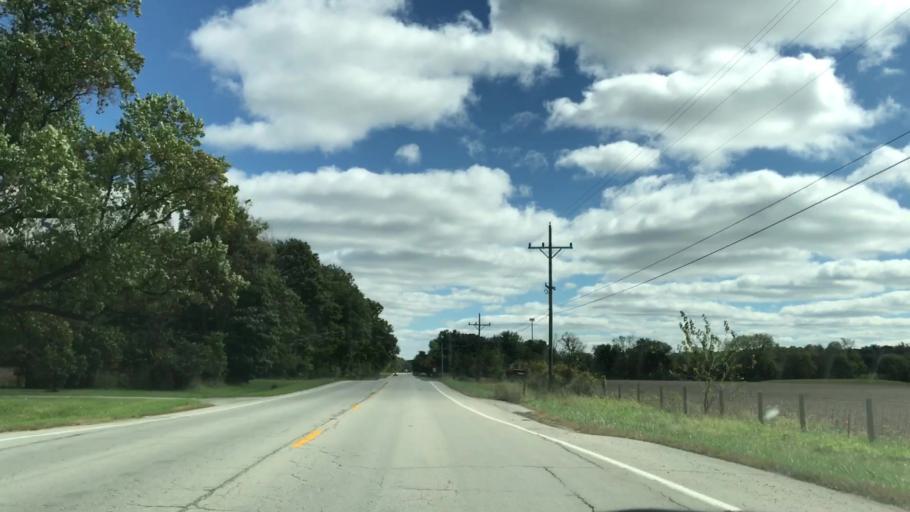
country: US
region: Indiana
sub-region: Hamilton County
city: Westfield
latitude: 40.0860
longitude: -86.1087
